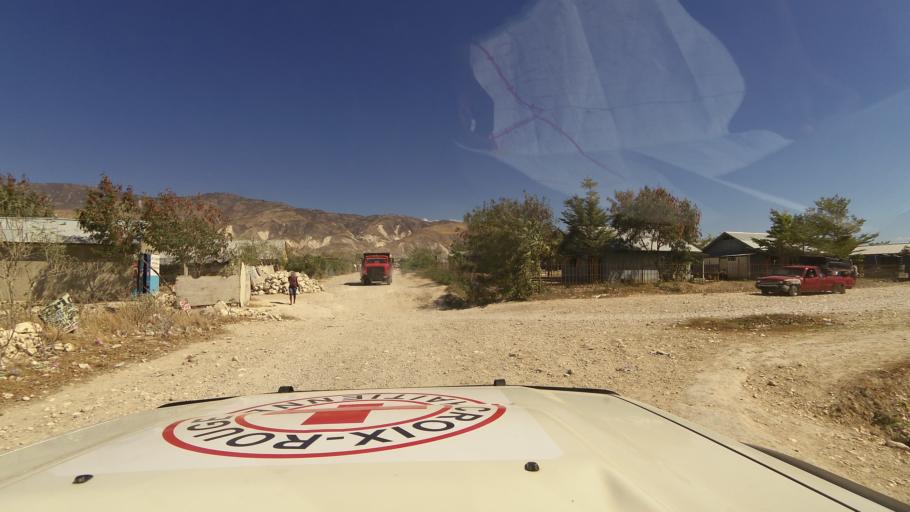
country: HT
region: Ouest
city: Croix des Bouquets
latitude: 18.6562
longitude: -72.2525
